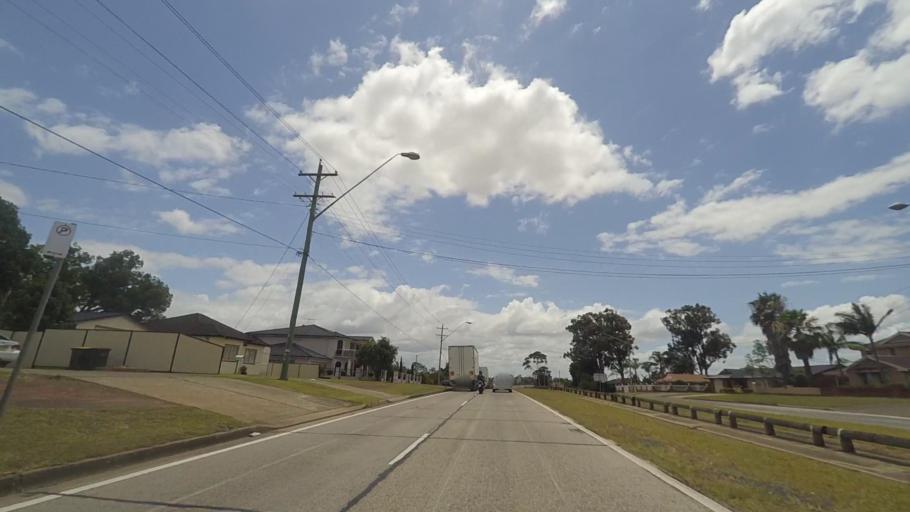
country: AU
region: New South Wales
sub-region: Fairfield
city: Fairfield Heights
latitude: -33.8655
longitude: 150.9259
